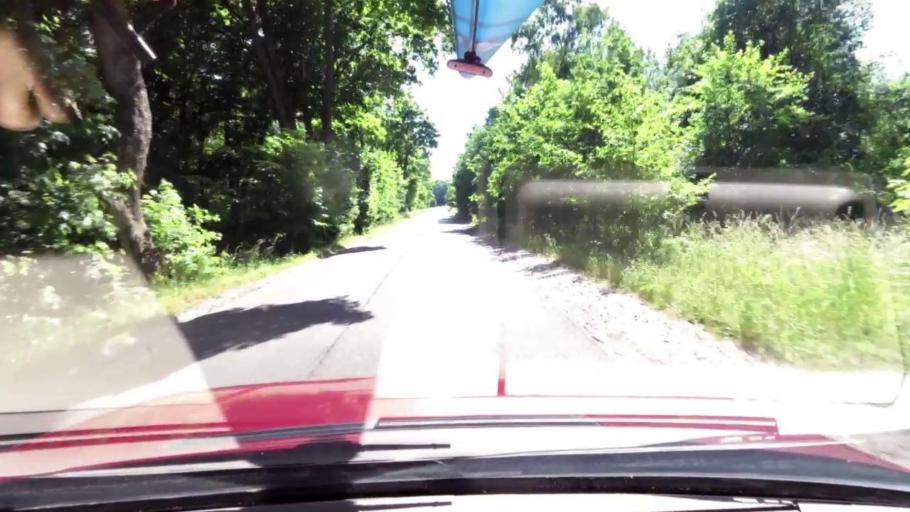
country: PL
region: Pomeranian Voivodeship
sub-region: Powiat slupski
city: Kobylnica
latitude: 54.3414
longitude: 16.9629
